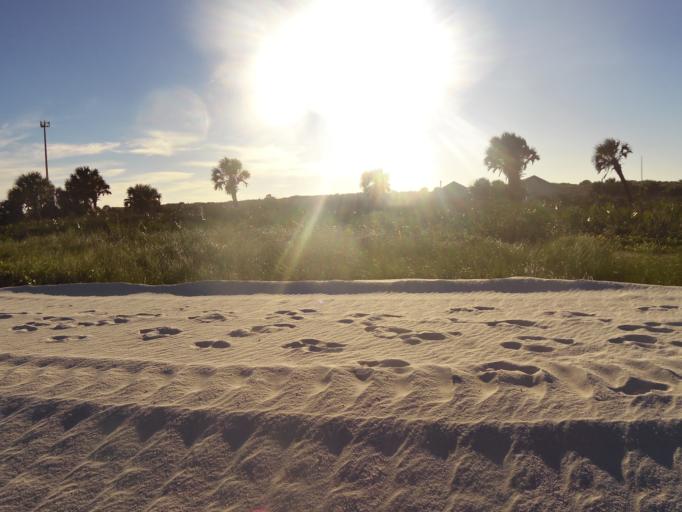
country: US
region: Florida
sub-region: Flagler County
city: Palm Coast
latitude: 29.6642
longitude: -81.2106
